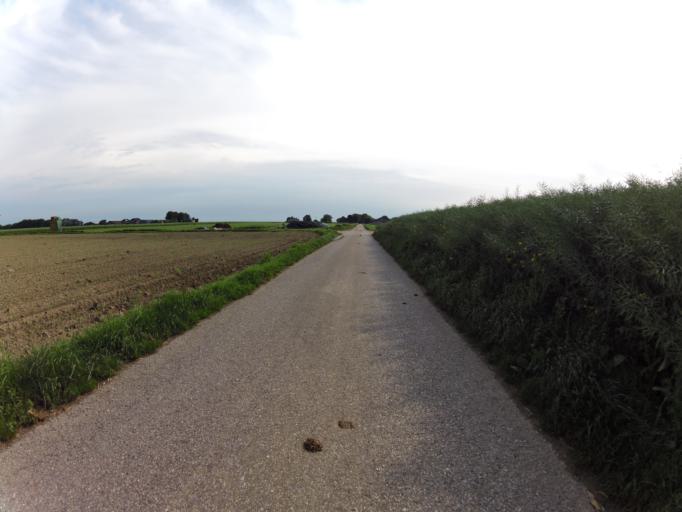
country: DE
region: North Rhine-Westphalia
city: Geilenkirchen
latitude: 50.9671
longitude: 6.1561
